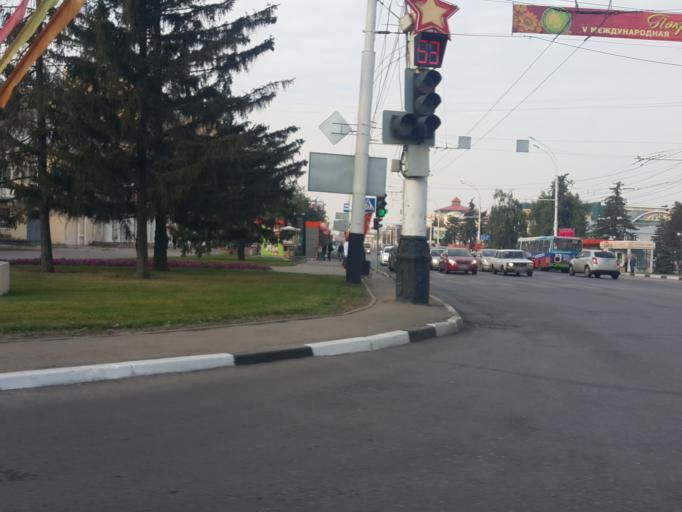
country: RU
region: Tambov
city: Tambov
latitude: 52.7211
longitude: 41.4516
